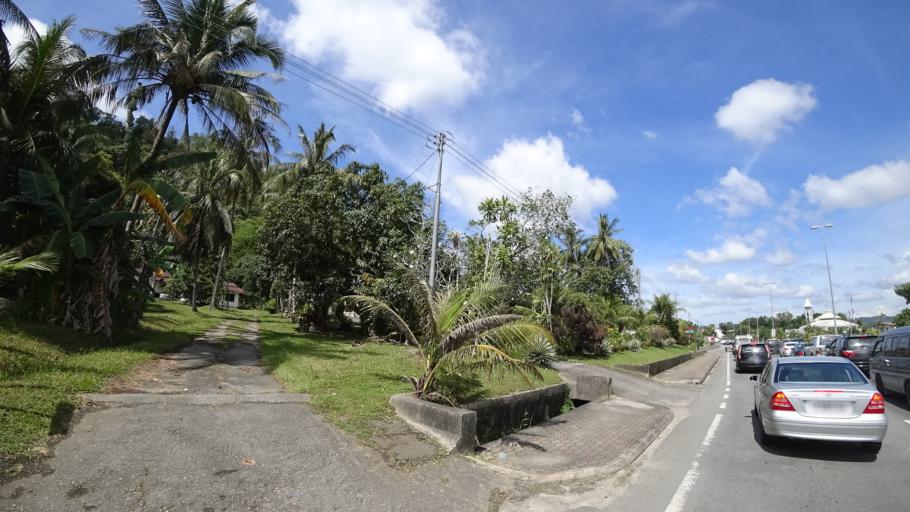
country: BN
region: Brunei and Muara
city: Bandar Seri Begawan
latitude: 4.8526
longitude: 114.8843
